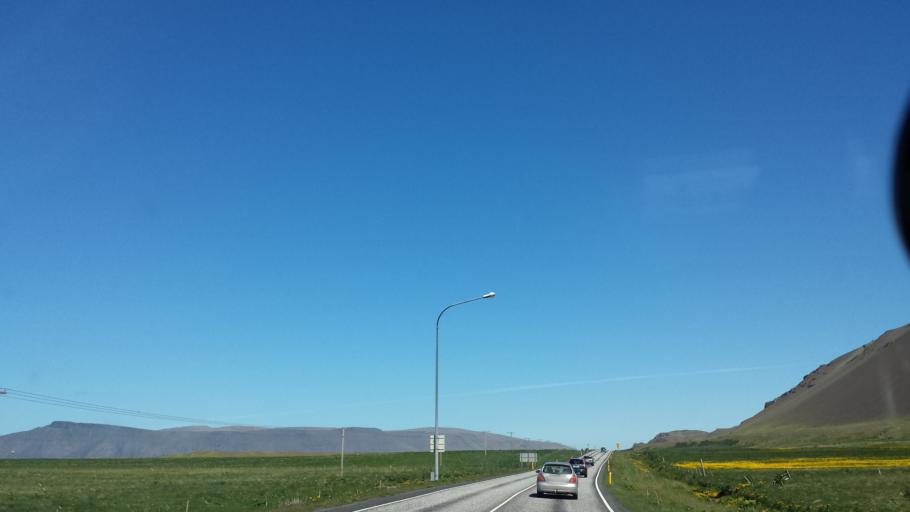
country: IS
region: Capital Region
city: Reykjavik
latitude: 64.2437
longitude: -21.8297
